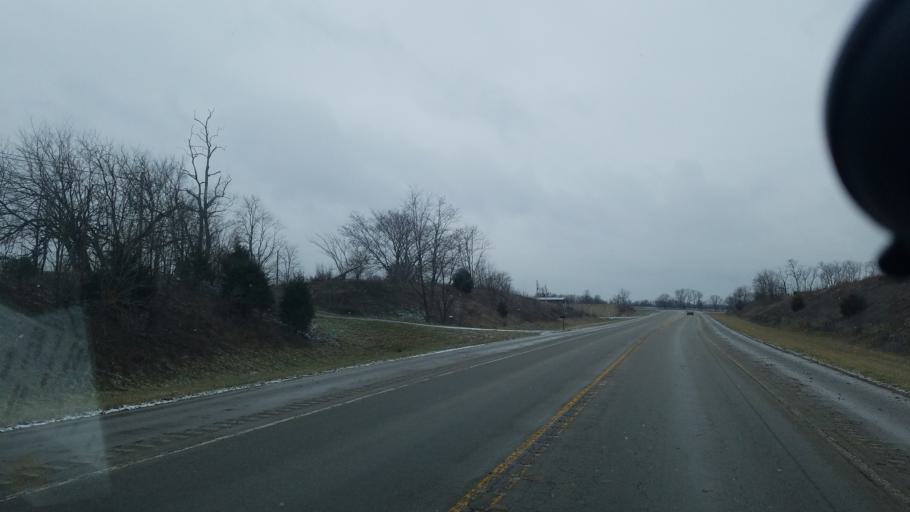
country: US
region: Kentucky
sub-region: Bath County
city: Owingsville
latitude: 38.2572
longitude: -83.8542
